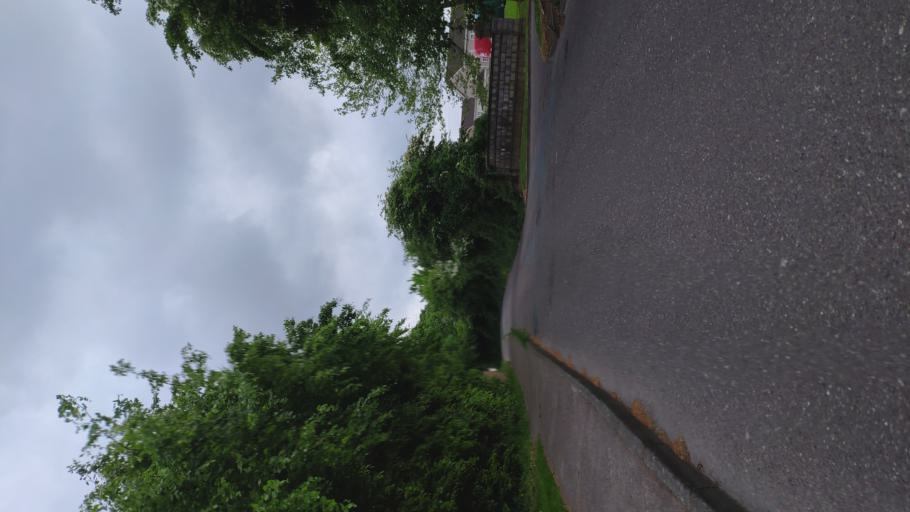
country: IE
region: Munster
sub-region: County Cork
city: Cork
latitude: 51.9247
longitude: -8.4589
